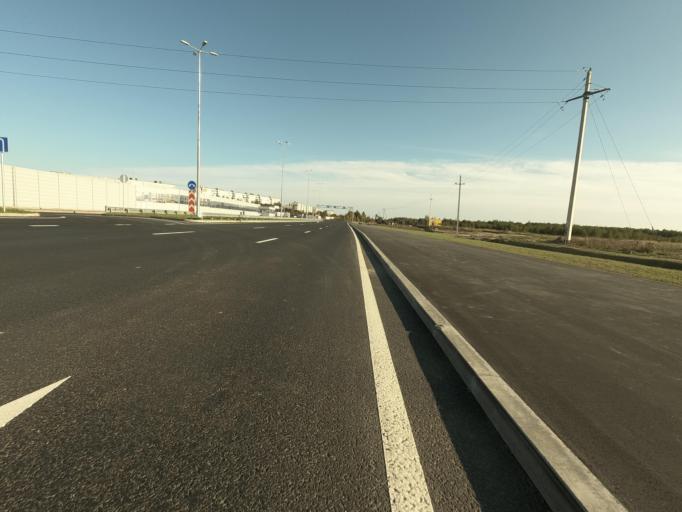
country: RU
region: St.-Petersburg
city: Kolpino
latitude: 59.7375
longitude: 30.5544
